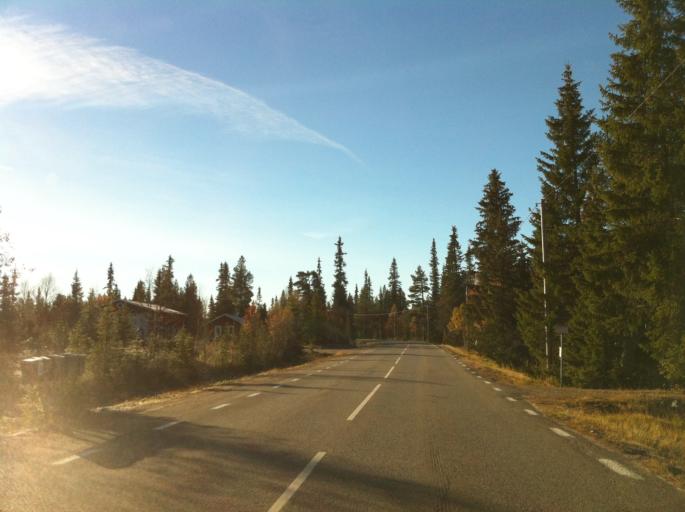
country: NO
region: Hedmark
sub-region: Engerdal
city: Engerdal
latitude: 62.0743
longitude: 12.3109
